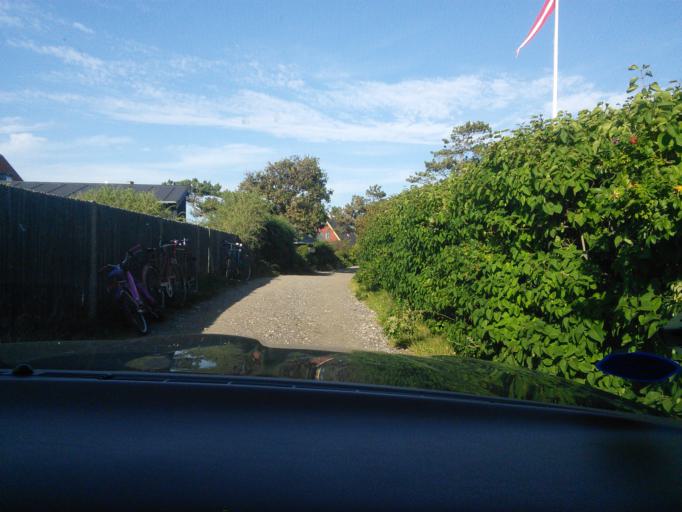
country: DK
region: Capital Region
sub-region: Halsnaes Kommune
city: Liseleje
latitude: 56.0129
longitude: 11.9585
